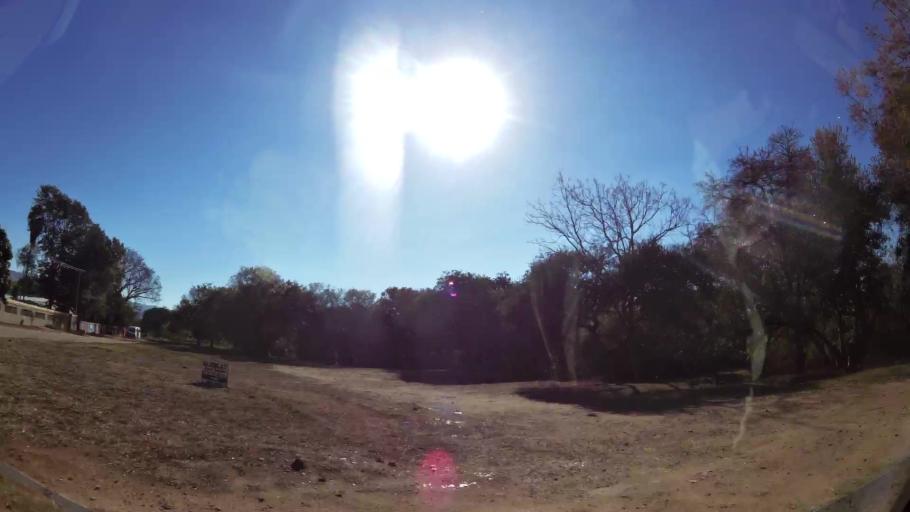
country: ZA
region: Limpopo
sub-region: Waterberg District Municipality
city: Mokopane
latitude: -24.1748
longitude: 29.0138
